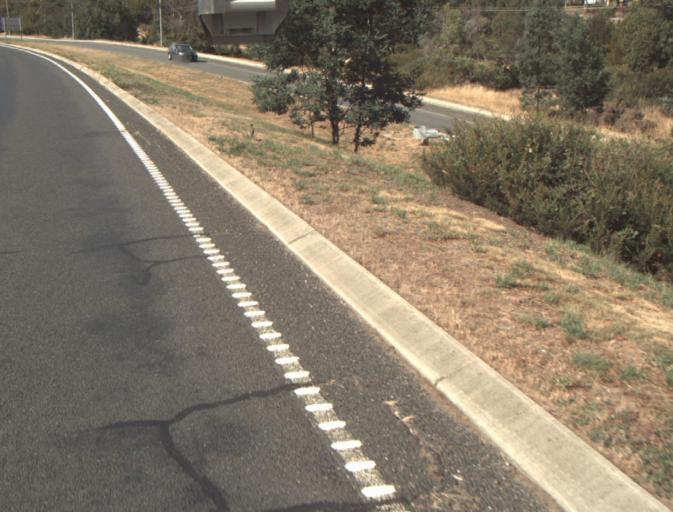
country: AU
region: Tasmania
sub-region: Launceston
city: Summerhill
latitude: -41.4730
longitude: 147.1427
